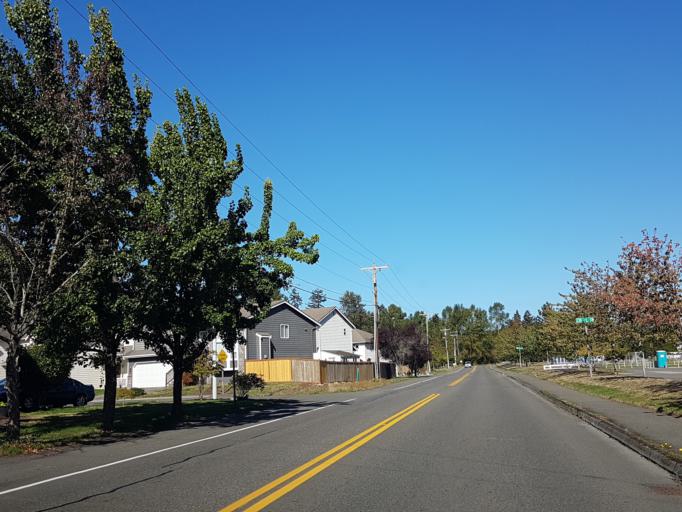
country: US
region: Washington
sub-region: Snohomish County
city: Brier
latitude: 47.7819
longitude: -122.2506
